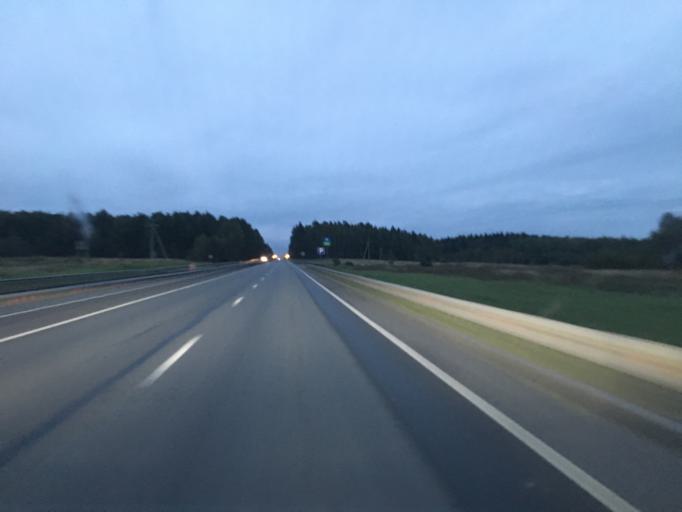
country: RU
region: Kaluga
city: Maloyaroslavets
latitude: 54.9673
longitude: 36.4740
